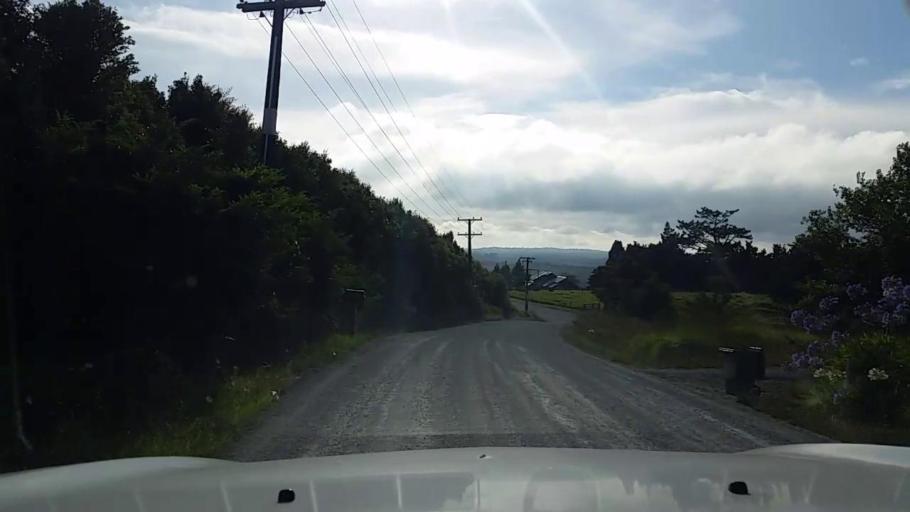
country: NZ
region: Northland
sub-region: Whangarei
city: Maungatapere
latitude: -35.6831
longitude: 174.1809
